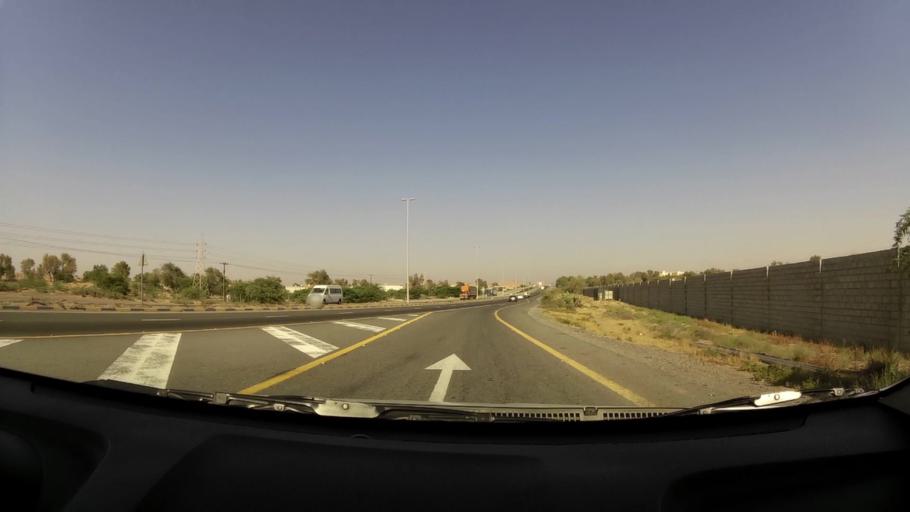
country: AE
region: Umm al Qaywayn
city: Umm al Qaywayn
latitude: 25.4439
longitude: 55.6291
